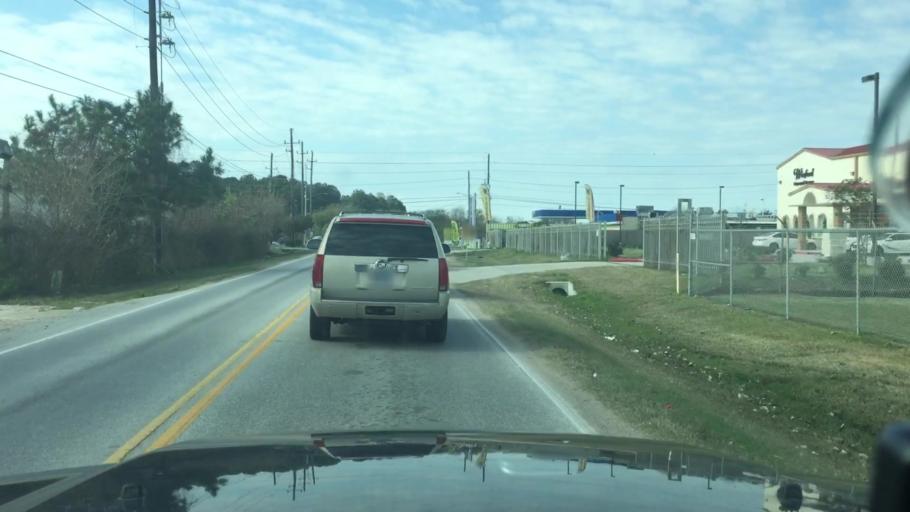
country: US
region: Texas
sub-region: Harris County
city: Hudson
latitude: 29.8981
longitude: -95.5233
